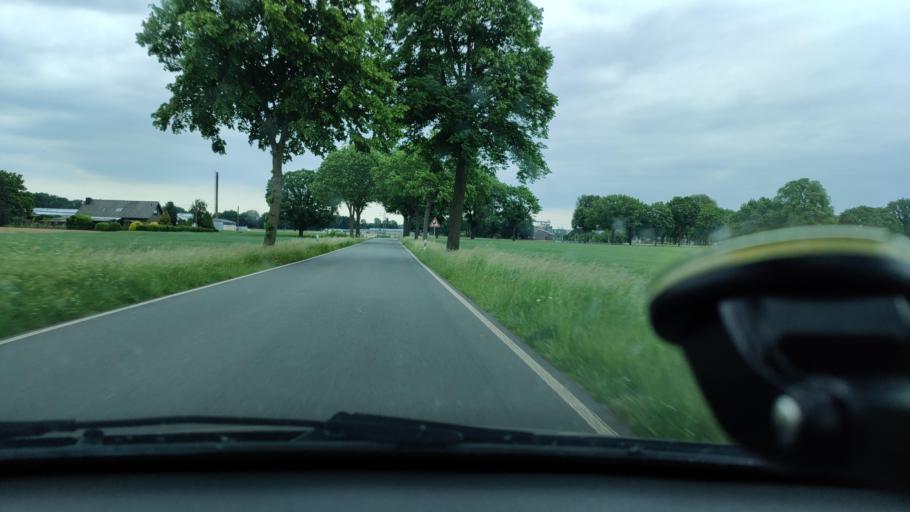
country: DE
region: North Rhine-Westphalia
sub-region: Regierungsbezirk Dusseldorf
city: Goch
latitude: 51.6832
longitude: 6.1073
